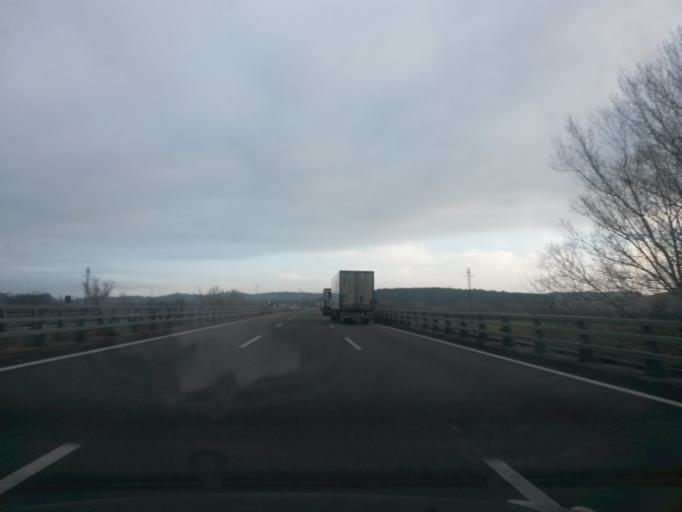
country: ES
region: Catalonia
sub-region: Provincia de Girona
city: Bascara
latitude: 42.1658
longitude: 2.9228
